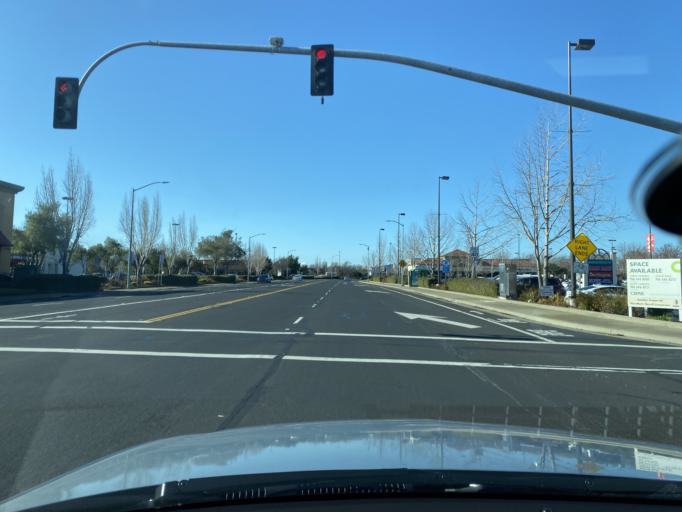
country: US
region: California
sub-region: Sacramento County
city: Elk Grove
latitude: 38.4254
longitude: -121.3928
